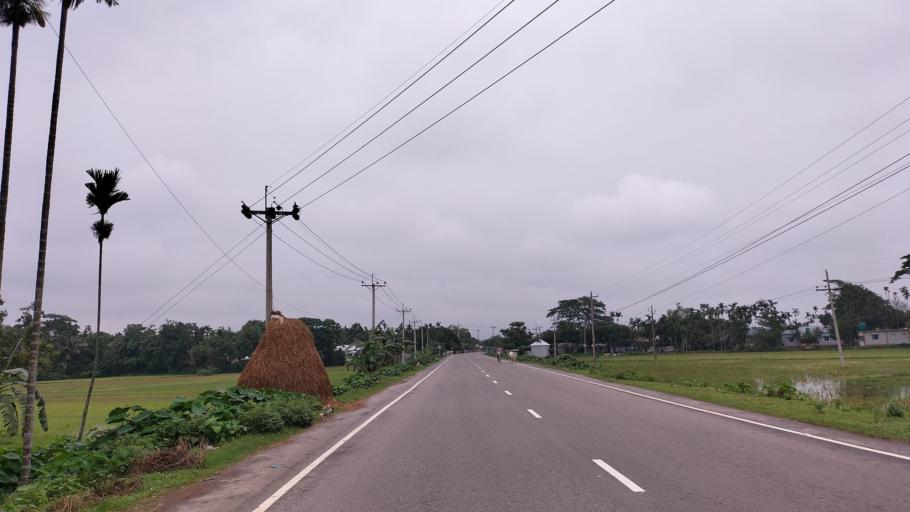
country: BD
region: Dhaka
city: Netrakona
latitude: 24.8515
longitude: 90.6481
